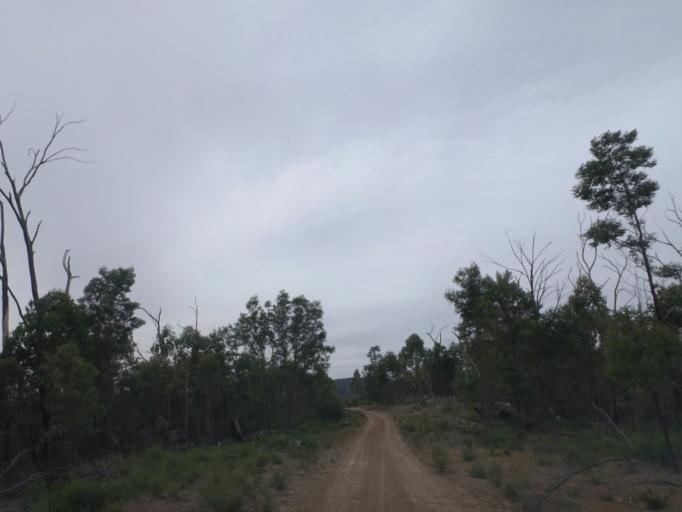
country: AU
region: Victoria
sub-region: Murrindindi
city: Alexandra
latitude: -37.3774
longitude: 145.5608
